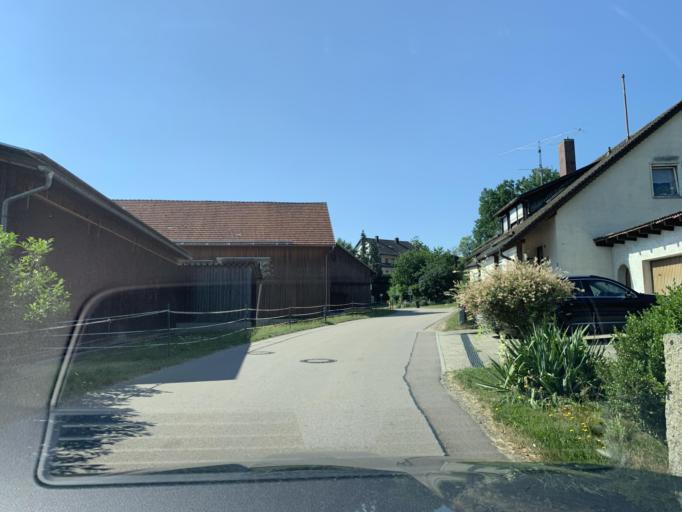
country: DE
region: Bavaria
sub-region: Upper Palatinate
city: Schwarzhofen
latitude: 49.3681
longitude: 12.3461
